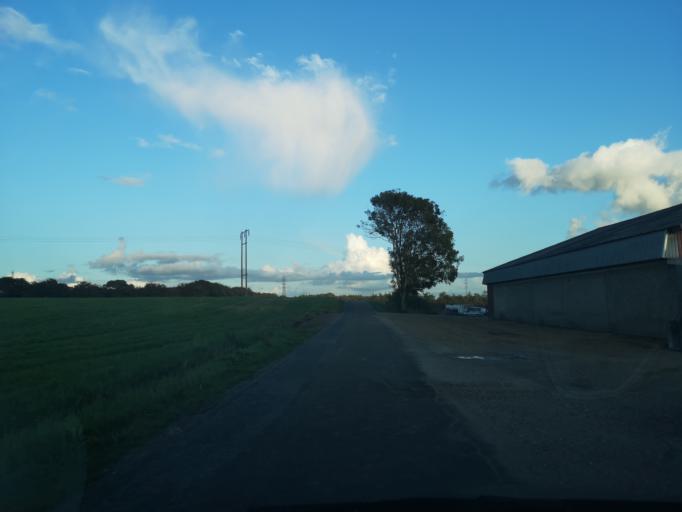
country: DK
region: Central Jutland
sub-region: Ringkobing-Skjern Kommune
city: Videbaek
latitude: 56.0441
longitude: 8.5840
